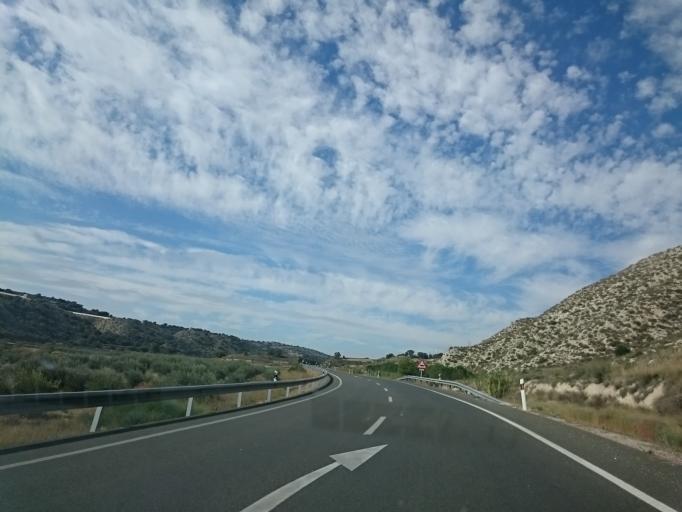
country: ES
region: Aragon
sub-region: Provincia de Huesca
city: Albelda
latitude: 41.8751
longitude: 0.5302
